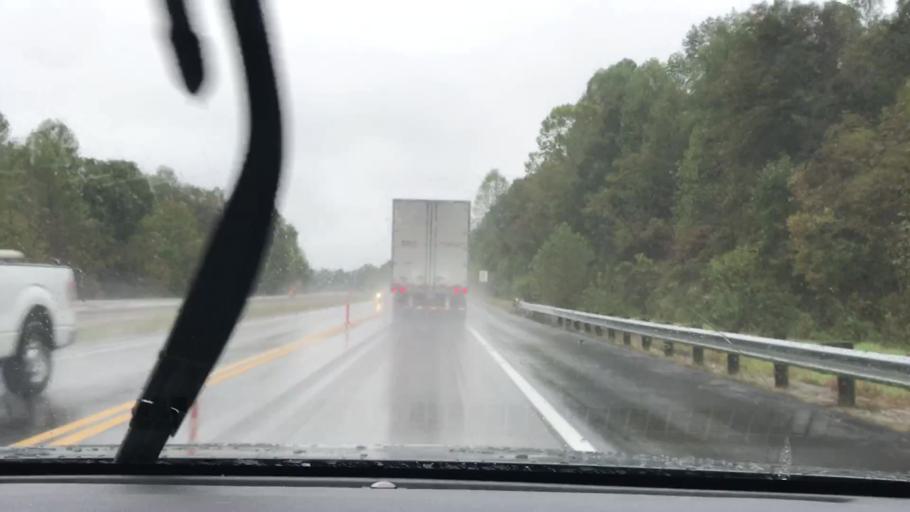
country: US
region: Kentucky
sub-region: Christian County
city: Hopkinsville
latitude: 36.9990
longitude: -87.4648
